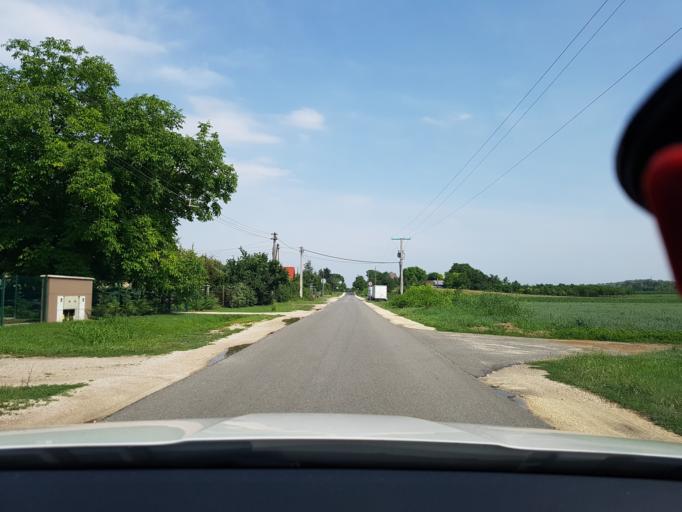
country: HU
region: Bacs-Kiskun
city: Kecskemet
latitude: 46.9249
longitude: 19.6442
